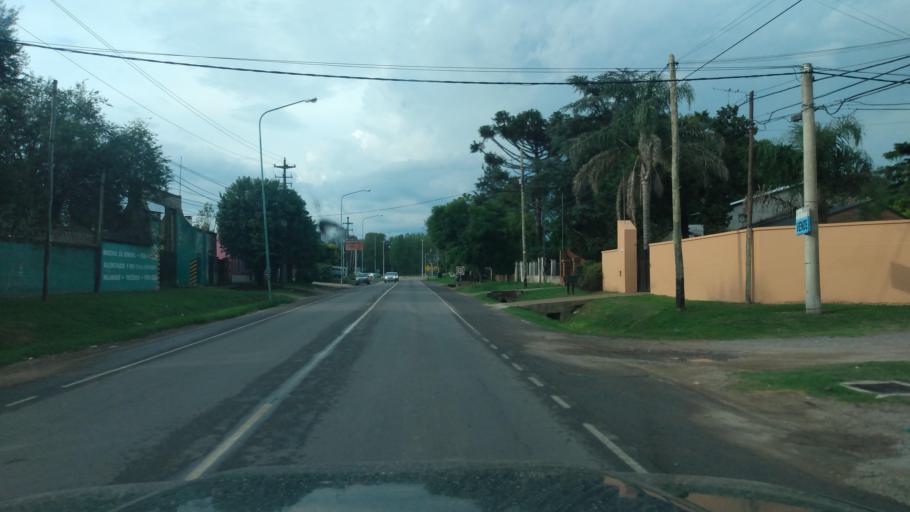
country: AR
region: Buenos Aires
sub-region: Partido de Lujan
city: Lujan
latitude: -34.5527
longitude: -59.1255
